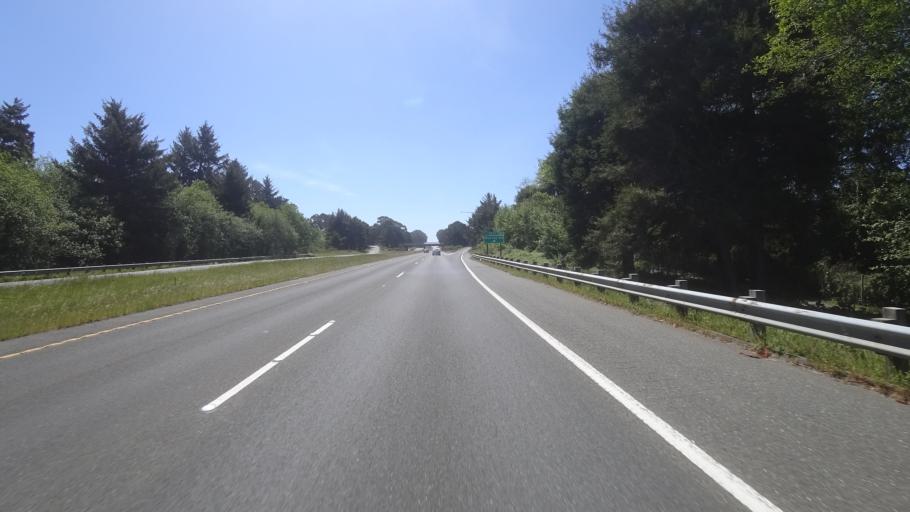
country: US
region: California
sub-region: Humboldt County
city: McKinleyville
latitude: 40.9598
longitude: -124.1162
